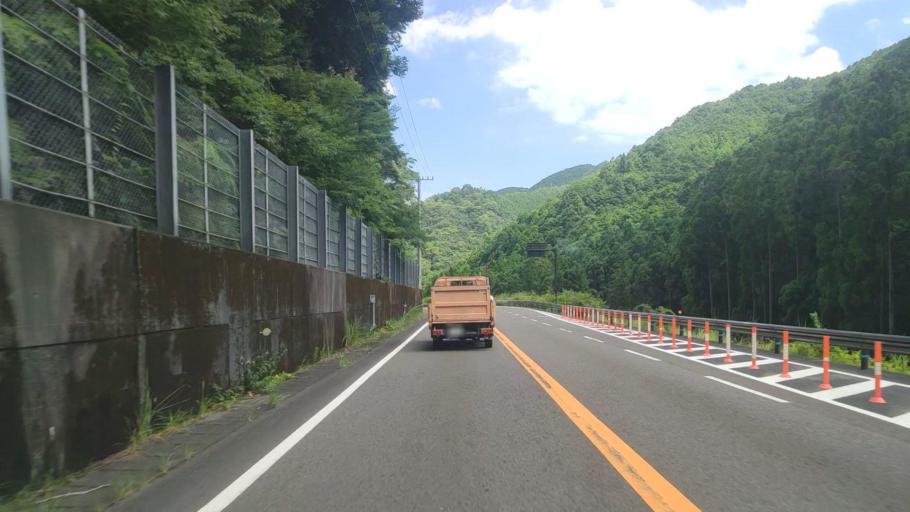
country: JP
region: Mie
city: Owase
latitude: 33.9249
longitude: 136.0930
